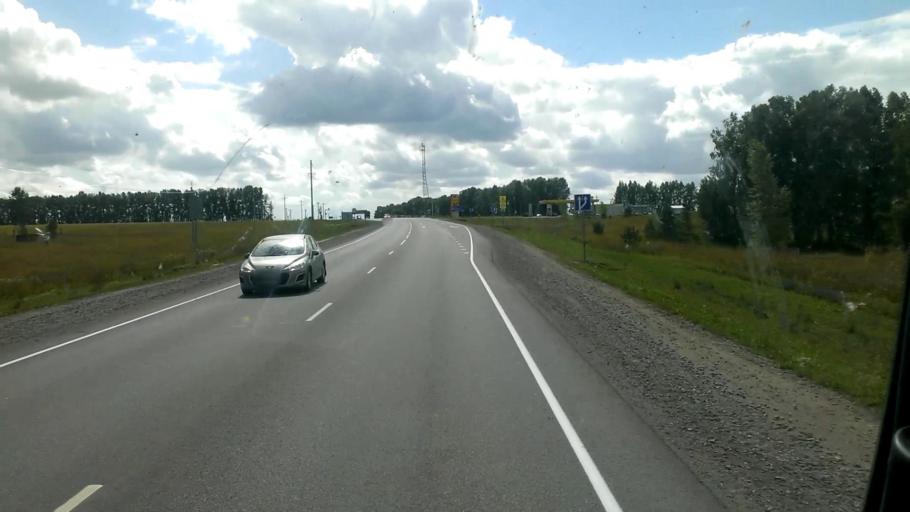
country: RU
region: Altai Krai
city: Troitskoye
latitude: 52.9705
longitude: 84.7487
